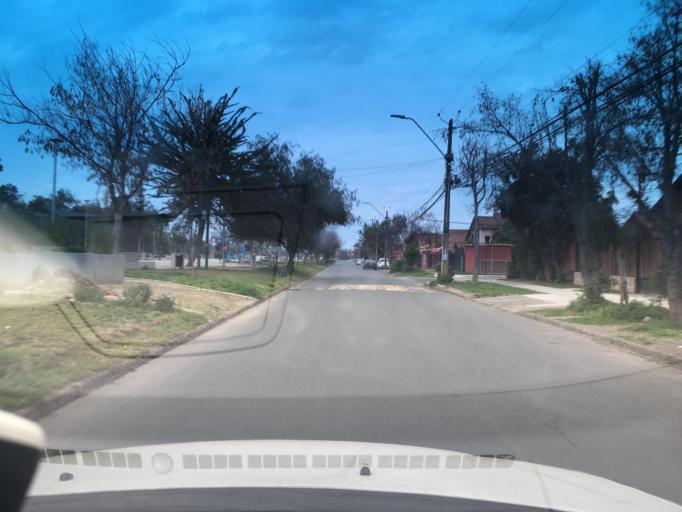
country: CL
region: Santiago Metropolitan
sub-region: Provincia de Santiago
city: Villa Presidente Frei, Nunoa, Santiago, Chile
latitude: -33.5002
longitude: -70.6054
